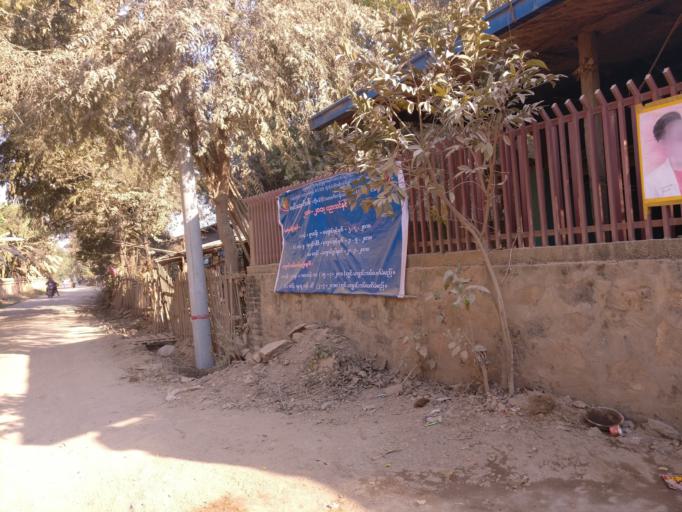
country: MM
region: Mandalay
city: Kyaukse
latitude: 21.7858
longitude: 96.1923
